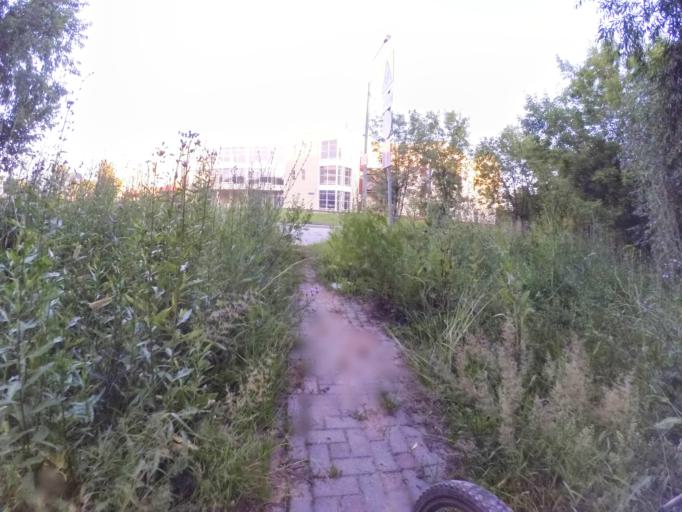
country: RU
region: Moscow
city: Strogino
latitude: 55.8261
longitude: 37.4177
